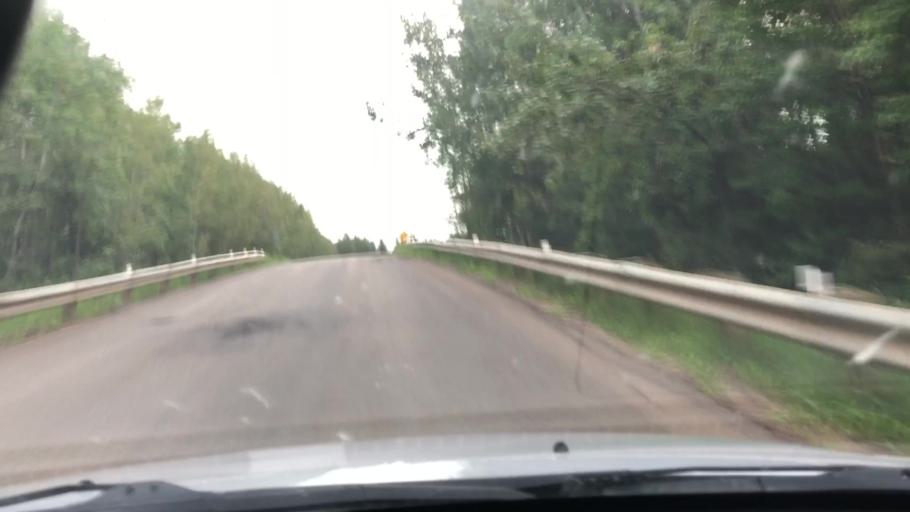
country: CA
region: Alberta
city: Devon
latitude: 53.4270
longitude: -113.6770
